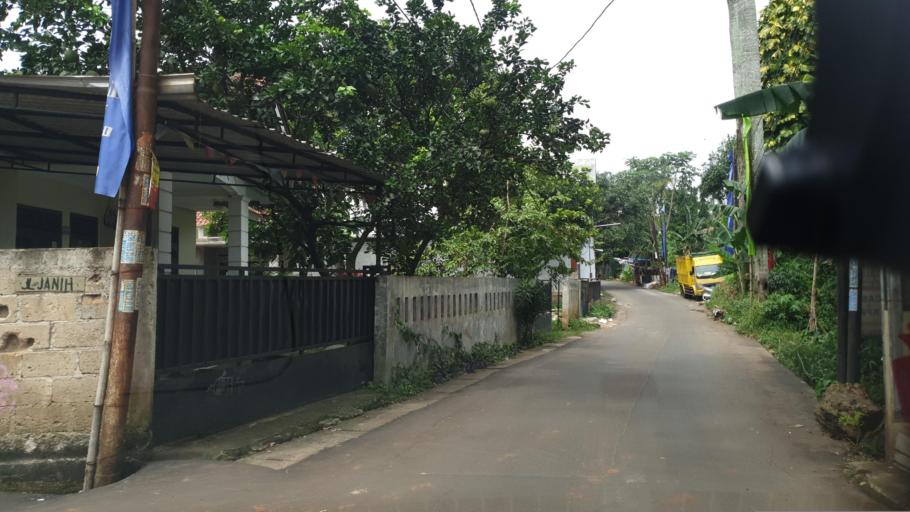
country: ID
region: West Java
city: Sawangan
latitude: -6.3773
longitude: 106.7632
